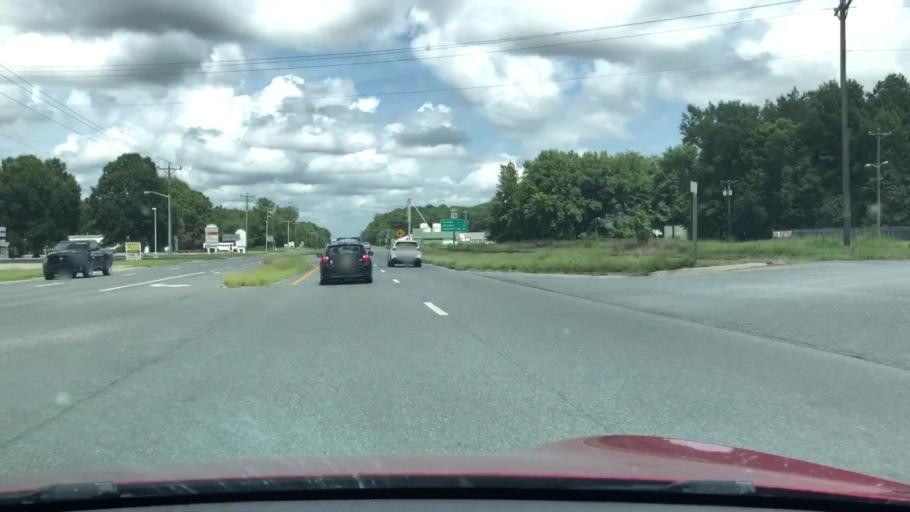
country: US
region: Virginia
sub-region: Northampton County
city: Exmore
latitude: 37.5489
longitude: -75.8094
